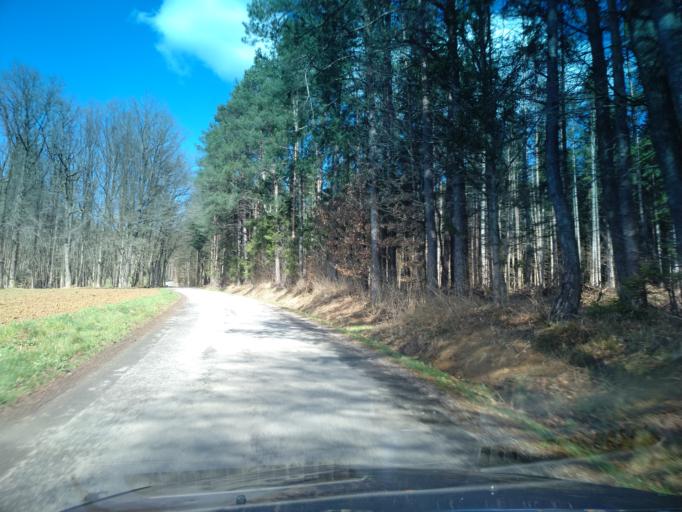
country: AT
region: Styria
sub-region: Politischer Bezirk Leibnitz
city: Sankt Johann im Saggautal
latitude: 46.7121
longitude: 15.3918
